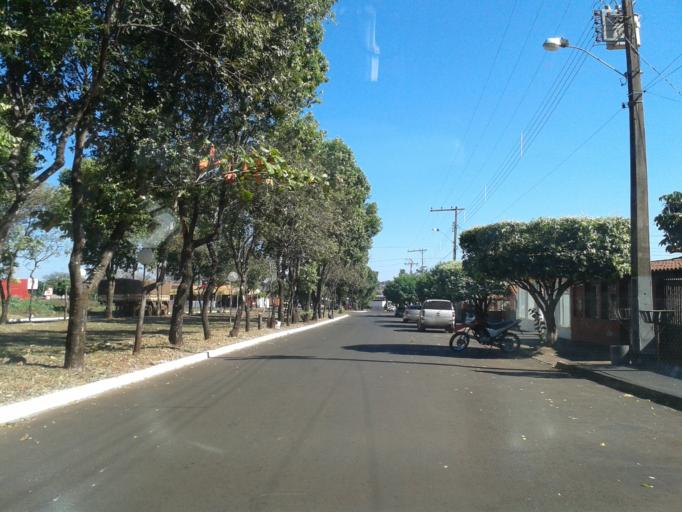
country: BR
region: Minas Gerais
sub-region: Santa Vitoria
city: Santa Vitoria
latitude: -18.8484
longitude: -50.1267
